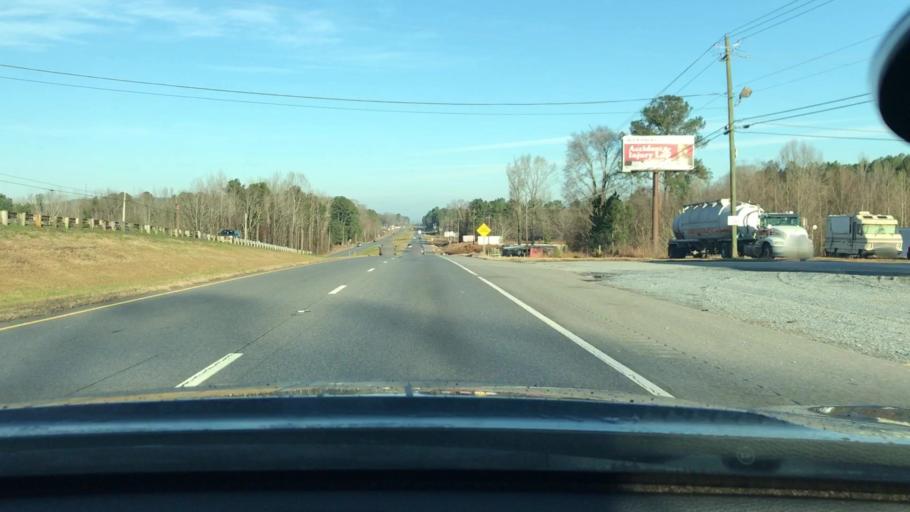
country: US
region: Alabama
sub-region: Talladega County
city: Childersburg
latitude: 33.2301
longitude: -86.3259
